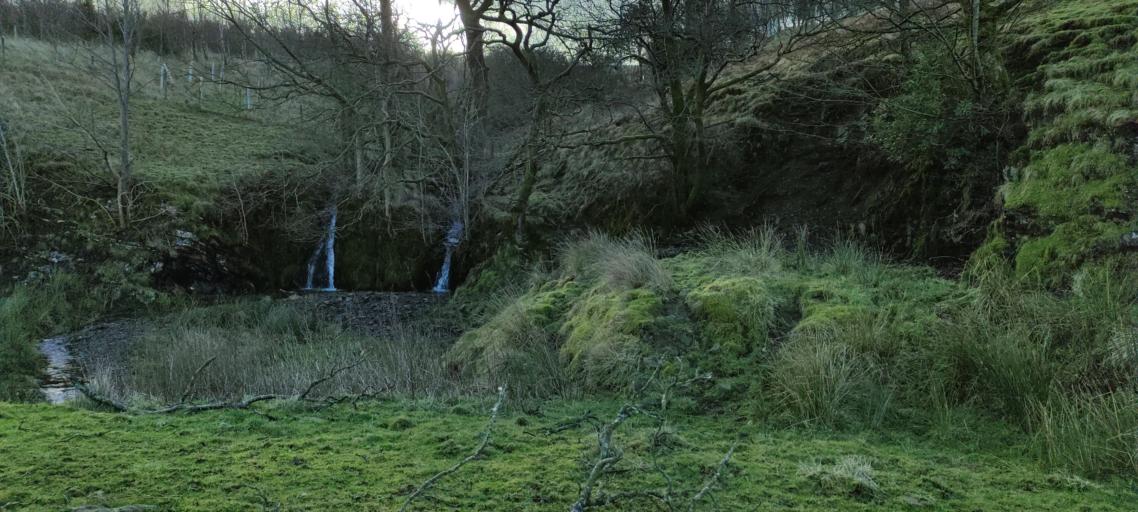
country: GB
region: Scotland
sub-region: Dumfries and Galloway
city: Langholm
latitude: 55.2100
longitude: -2.9654
